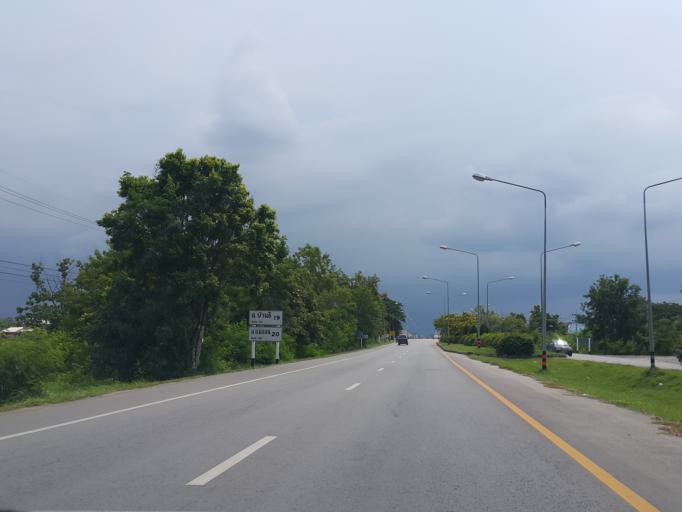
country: TH
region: Chiang Mai
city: San Kamphaeng
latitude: 18.7228
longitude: 99.1080
